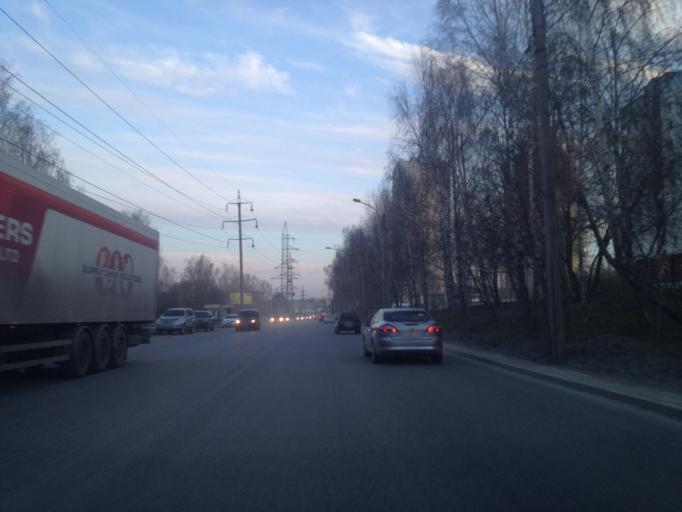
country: RU
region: Sverdlovsk
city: Sovkhoznyy
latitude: 56.7797
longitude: 60.5985
